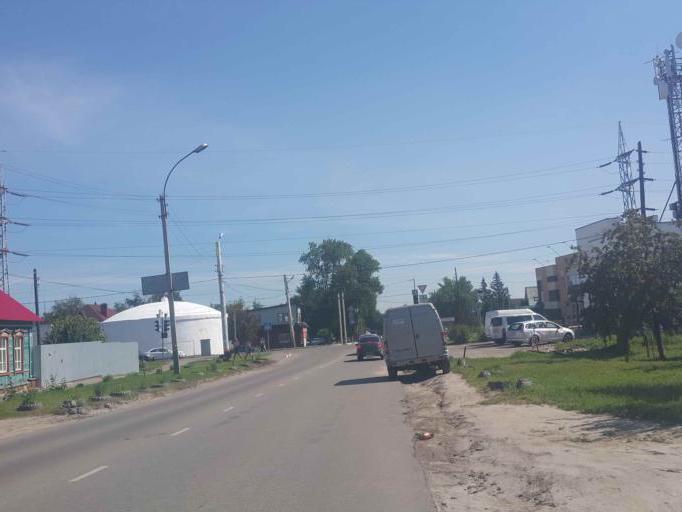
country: RU
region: Tambov
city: Pokrovo-Prigorodnoye
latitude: 52.7088
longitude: 41.4174
